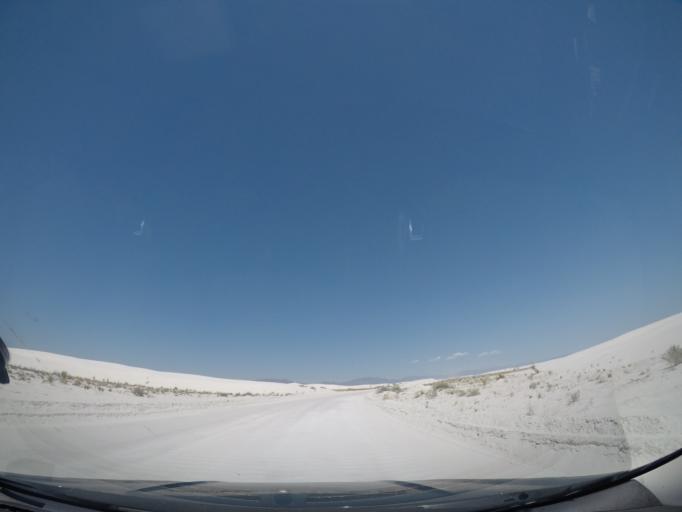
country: US
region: New Mexico
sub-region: Otero County
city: Holloman Air Force Base
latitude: 32.7986
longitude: -106.2510
